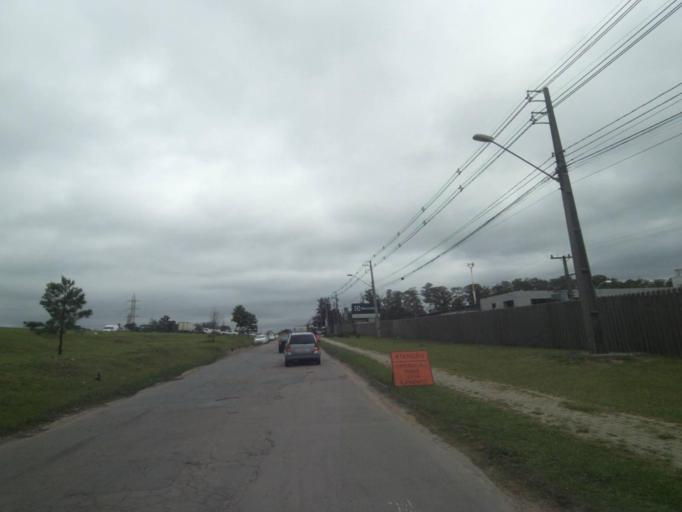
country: BR
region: Parana
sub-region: Araucaria
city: Araucaria
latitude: -25.5510
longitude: -49.3287
